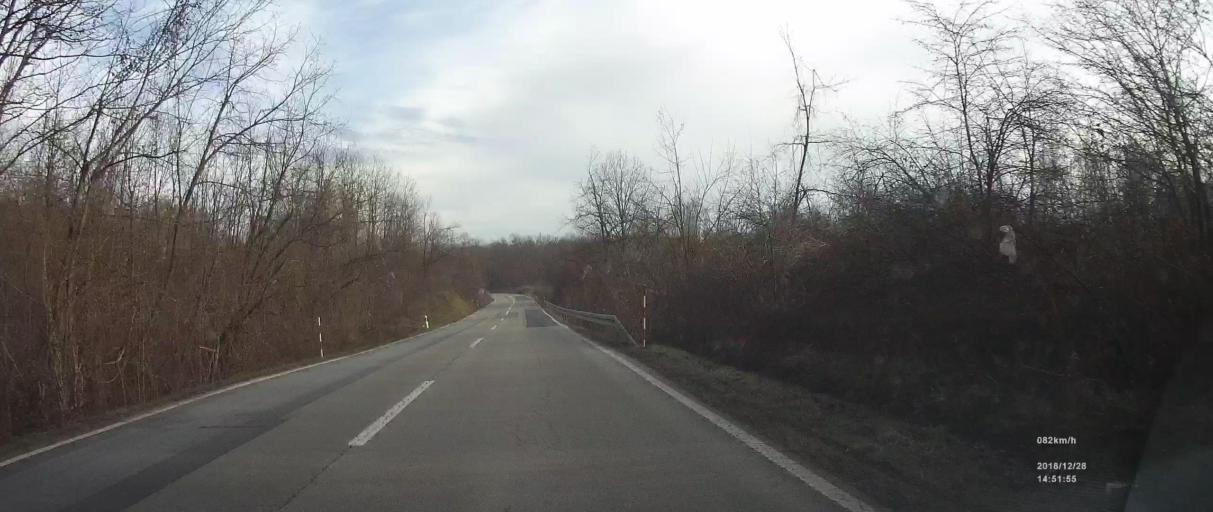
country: HR
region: Karlovacka
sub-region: Grad Karlovac
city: Karlovac
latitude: 45.4456
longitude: 15.3901
